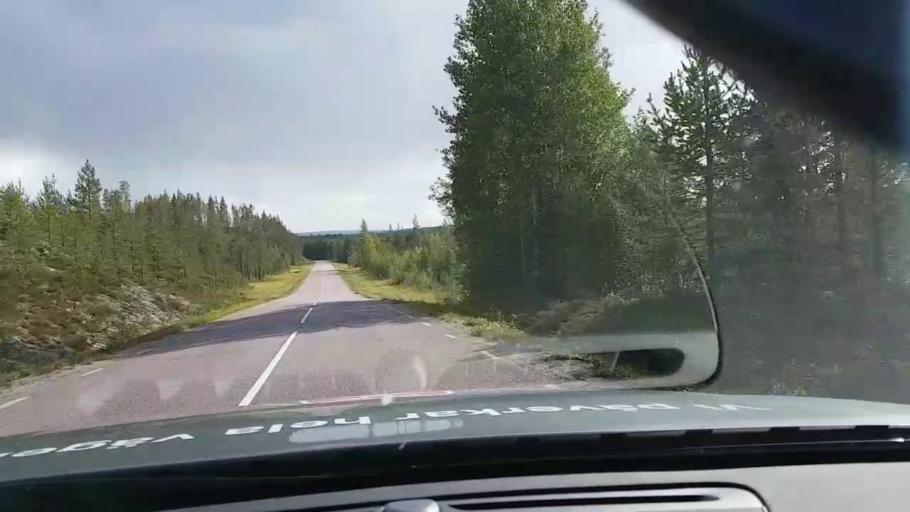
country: SE
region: Vaesterbotten
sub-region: Asele Kommun
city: Asele
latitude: 63.8712
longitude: 17.3570
